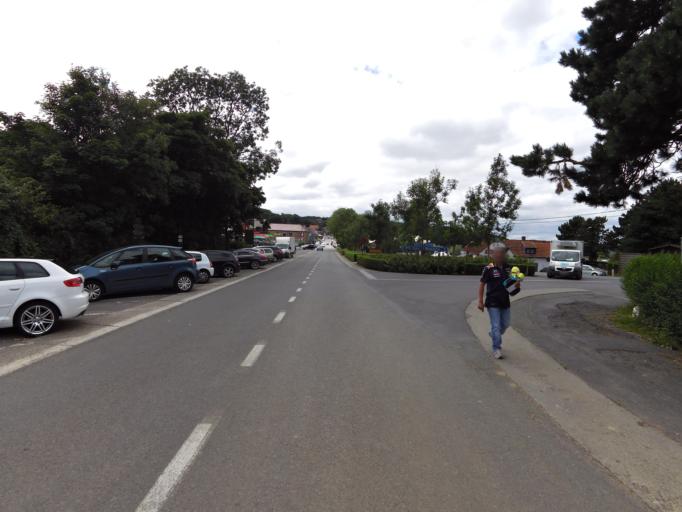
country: FR
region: Nord-Pas-de-Calais
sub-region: Departement du Nord
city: Saint-Jans-Cappel
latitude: 50.7830
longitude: 2.7444
